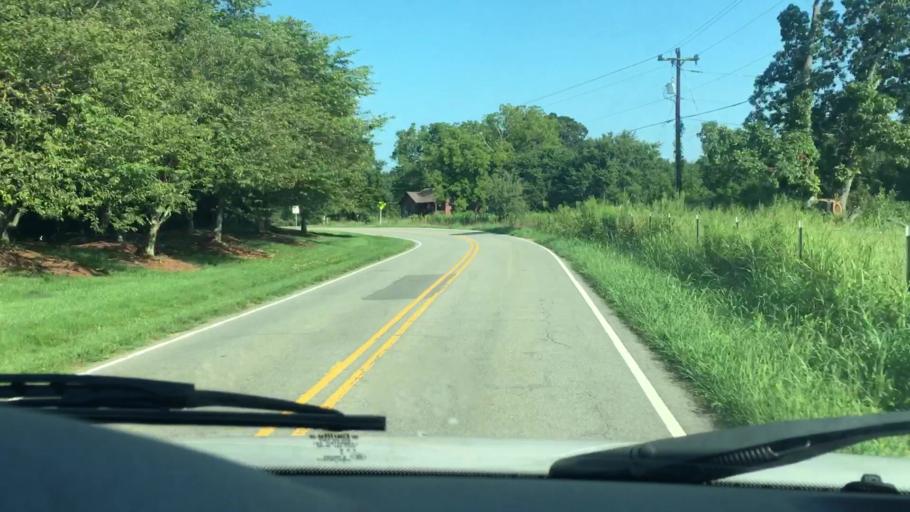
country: US
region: North Carolina
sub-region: Mecklenburg County
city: Huntersville
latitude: 35.4385
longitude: -80.8168
